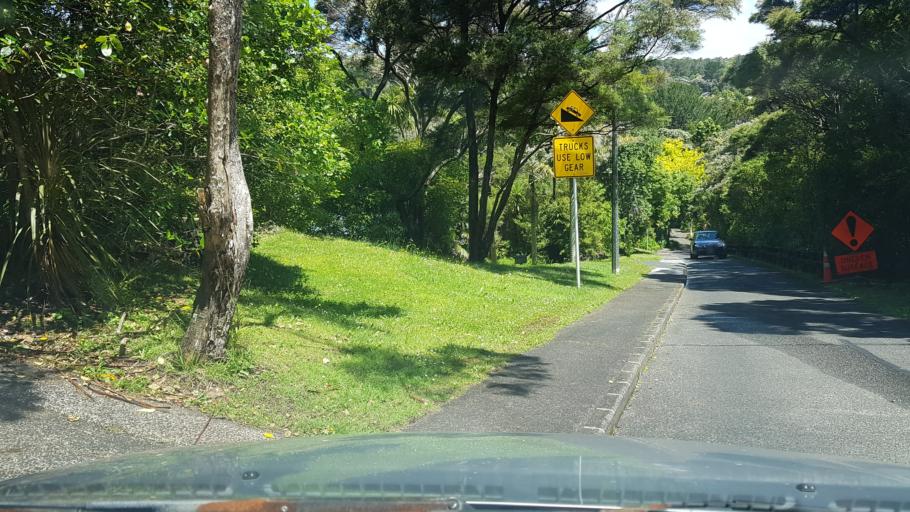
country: NZ
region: Auckland
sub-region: Auckland
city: North Shore
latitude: -36.8109
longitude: 174.7048
